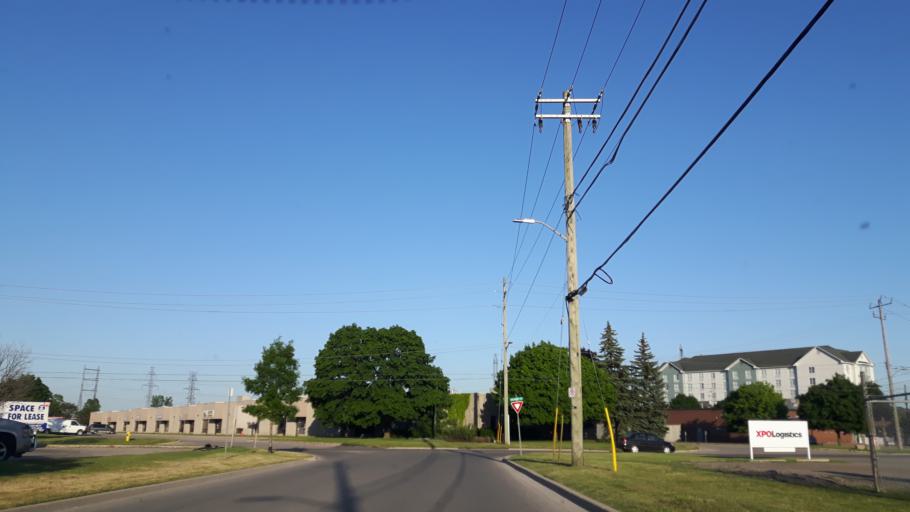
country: CA
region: Ontario
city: London
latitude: 42.9293
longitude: -81.2137
